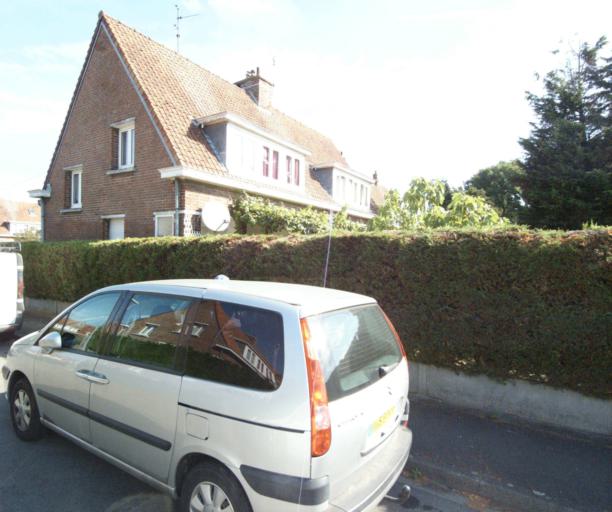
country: FR
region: Nord-Pas-de-Calais
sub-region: Departement du Nord
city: Halluin
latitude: 50.7766
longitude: 3.1361
